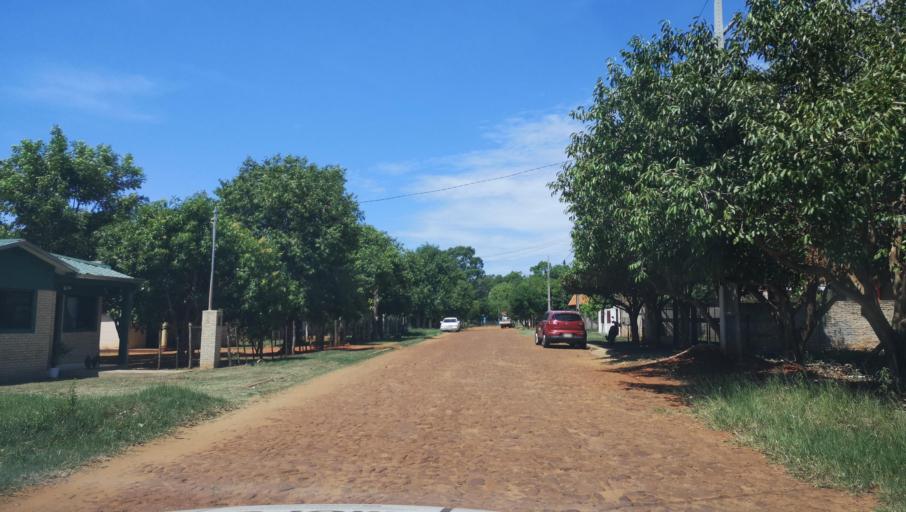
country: PY
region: Misiones
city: Santa Maria
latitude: -26.8971
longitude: -57.0308
